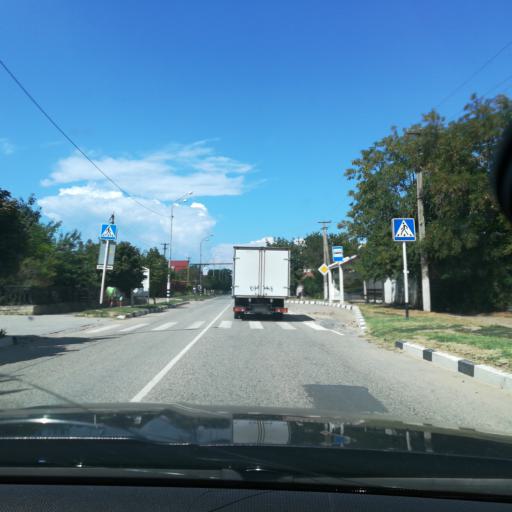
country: RU
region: Krasnodarskiy
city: Taman'
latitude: 45.2173
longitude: 36.7309
